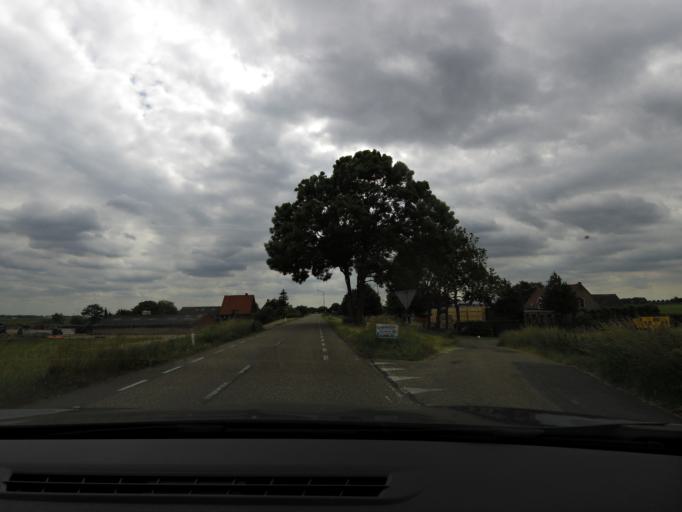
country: NL
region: North Brabant
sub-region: Gemeente Moerdijk
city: Klundert
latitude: 51.6555
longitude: 4.4881
